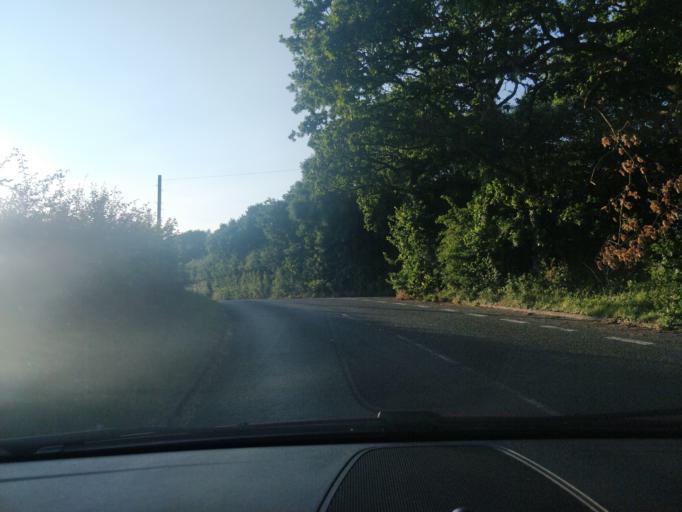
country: GB
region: England
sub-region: Lancashire
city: Parbold
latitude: 53.6100
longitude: -2.7793
